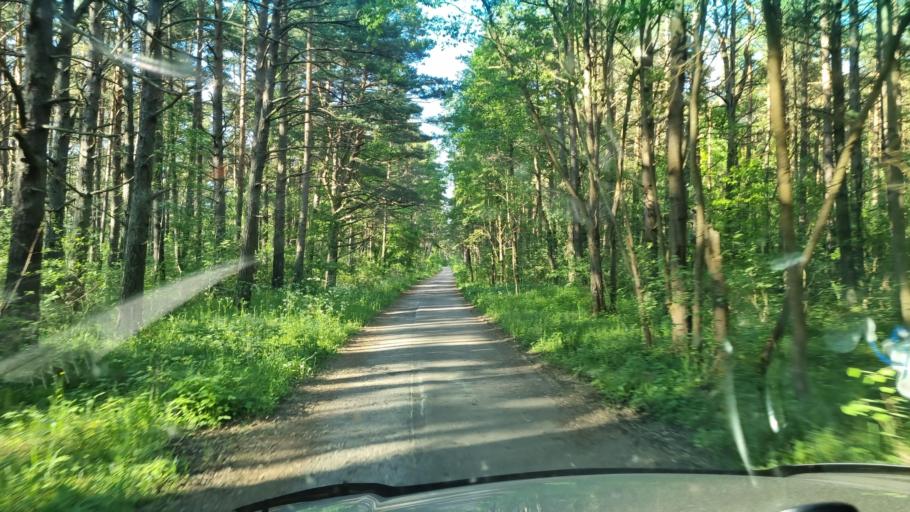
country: LV
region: Ventspils
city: Ventspils
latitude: 57.3745
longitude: 21.5262
